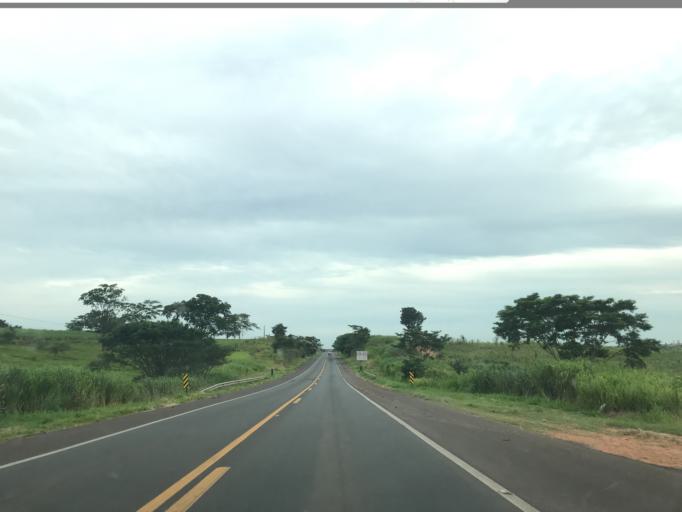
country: BR
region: Sao Paulo
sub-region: Birigui
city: Birigui
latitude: -21.5923
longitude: -50.4616
